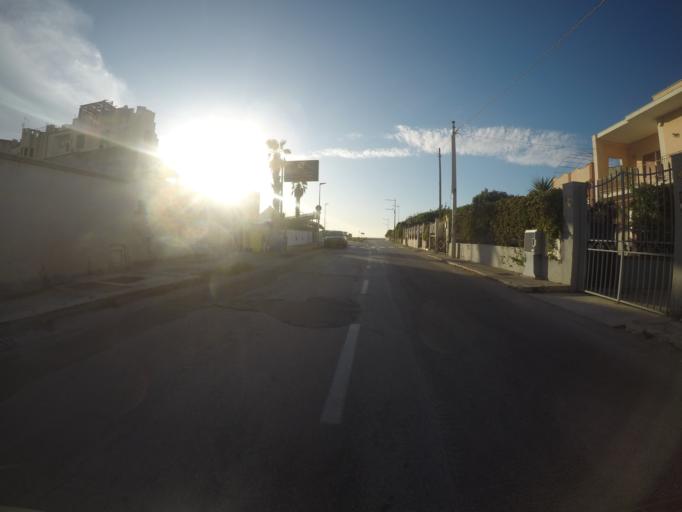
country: IT
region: Sicily
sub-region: Palermo
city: Isola delle Femmine
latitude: 38.1993
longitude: 13.2448
